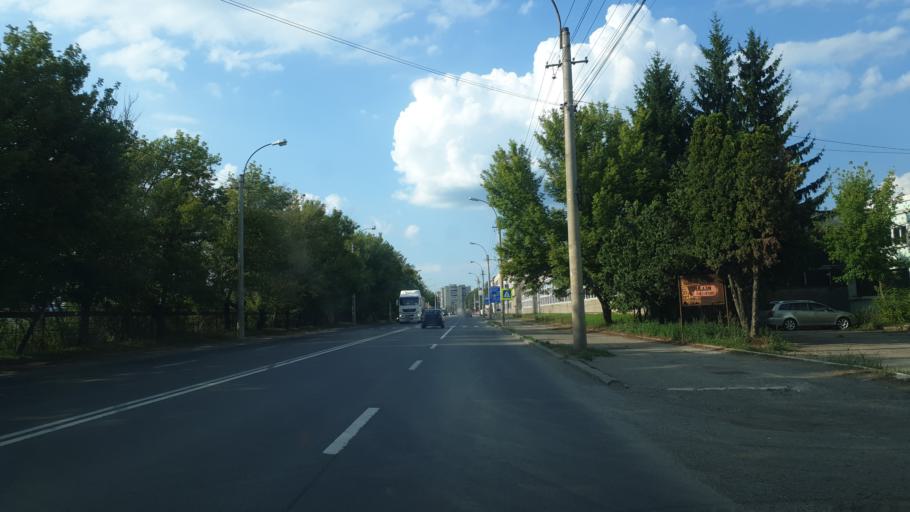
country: RO
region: Covasna
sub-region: Municipiul Sfantu Gheorghe
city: Sfantu-Gheorghe
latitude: 45.8534
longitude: 25.8064
